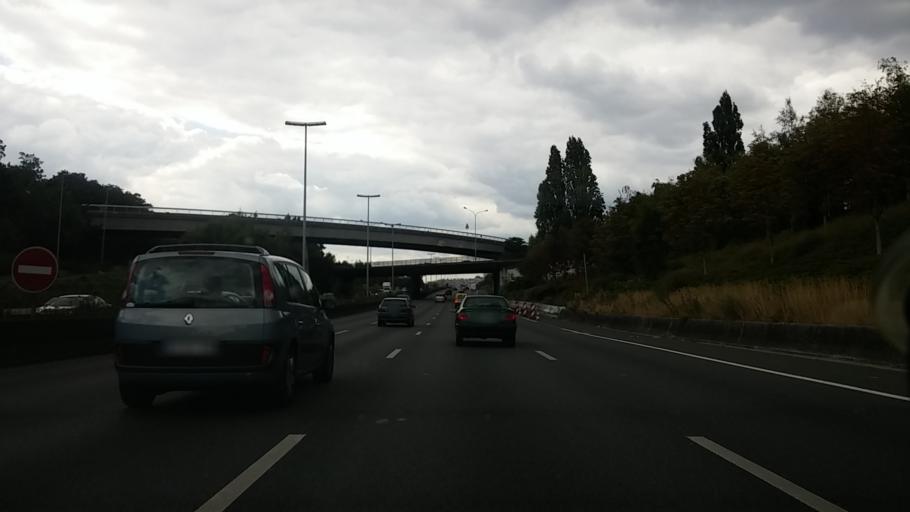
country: FR
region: Ile-de-France
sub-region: Departement de Seine-Saint-Denis
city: Romainville
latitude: 48.8767
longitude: 2.4429
